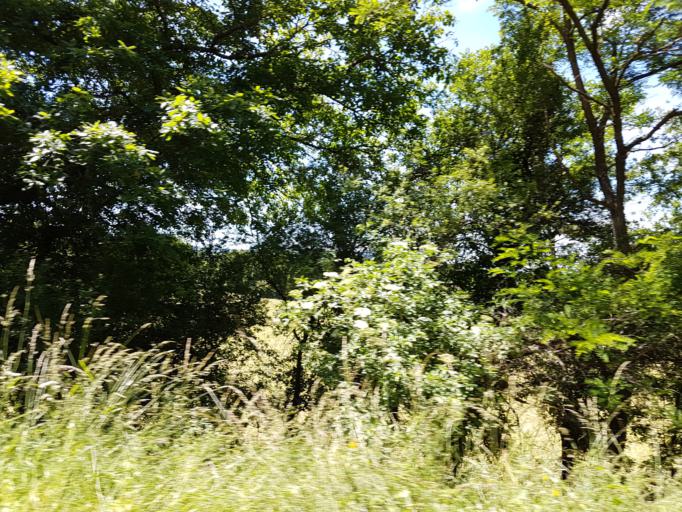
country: FR
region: Bourgogne
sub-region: Departement de Saone-et-Loire
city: Epinac
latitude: 46.9923
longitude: 4.5079
